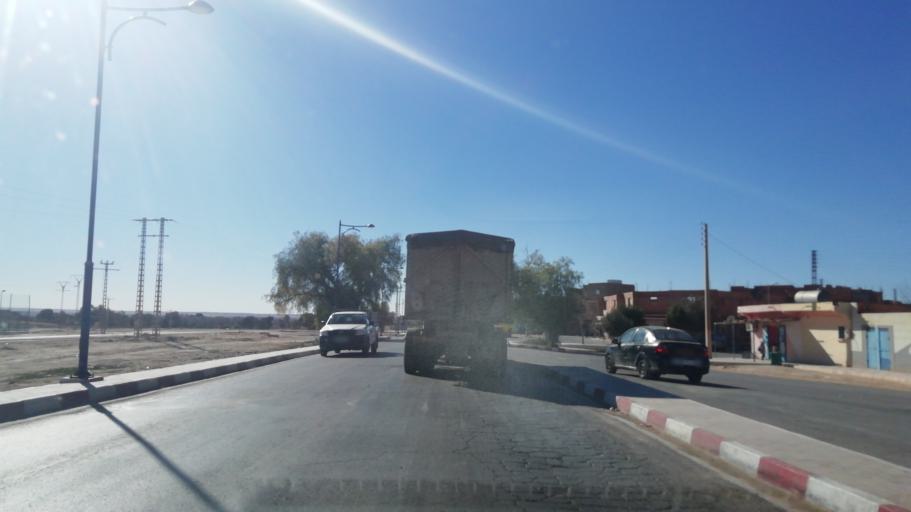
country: DZ
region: Saida
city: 'Ain el Hadjar
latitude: 34.1520
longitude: 0.0698
